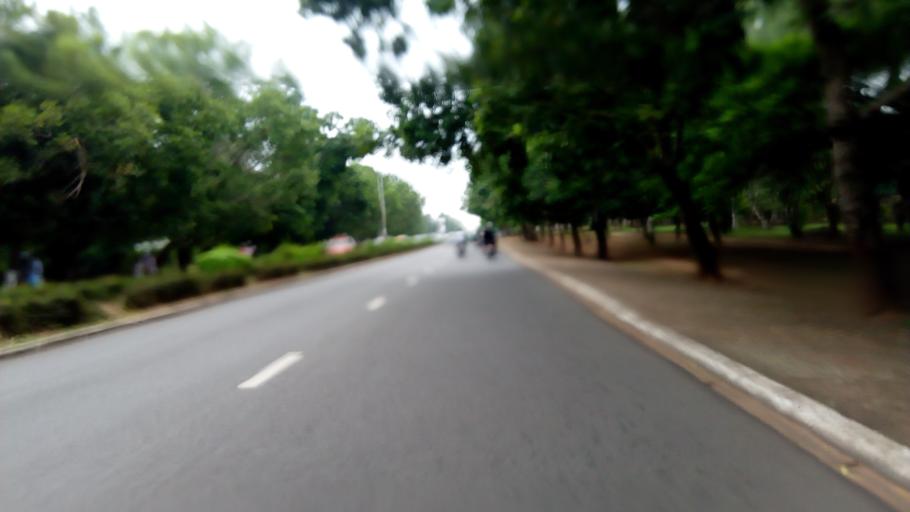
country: TG
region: Maritime
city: Lome
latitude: 6.1741
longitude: 1.2184
